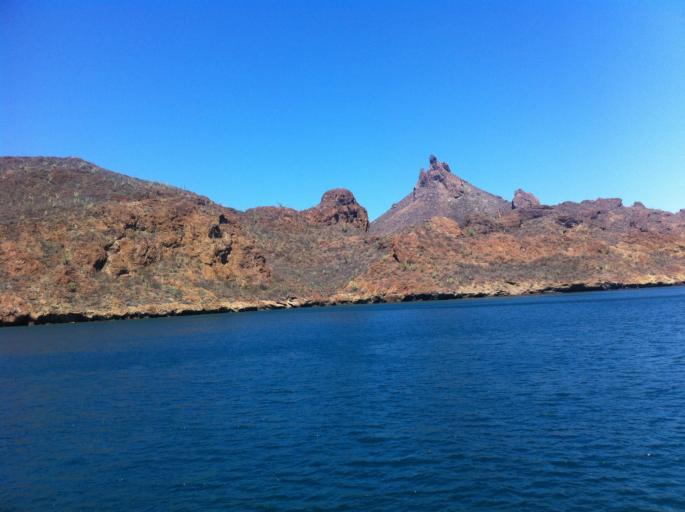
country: MX
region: Sonora
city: Heroica Guaymas
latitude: 27.9375
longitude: -111.0583
